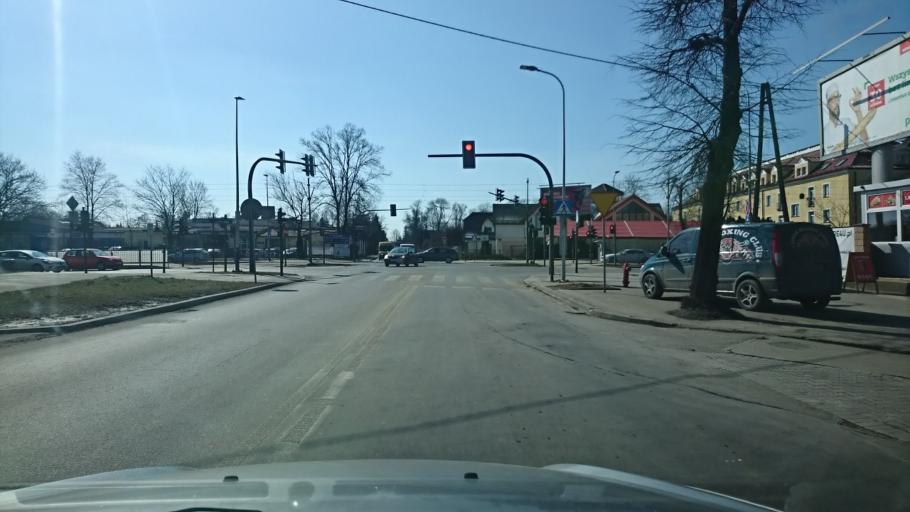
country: PL
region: Lesser Poland Voivodeship
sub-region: Powiat wielicki
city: Kokotow
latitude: 50.0690
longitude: 20.0527
